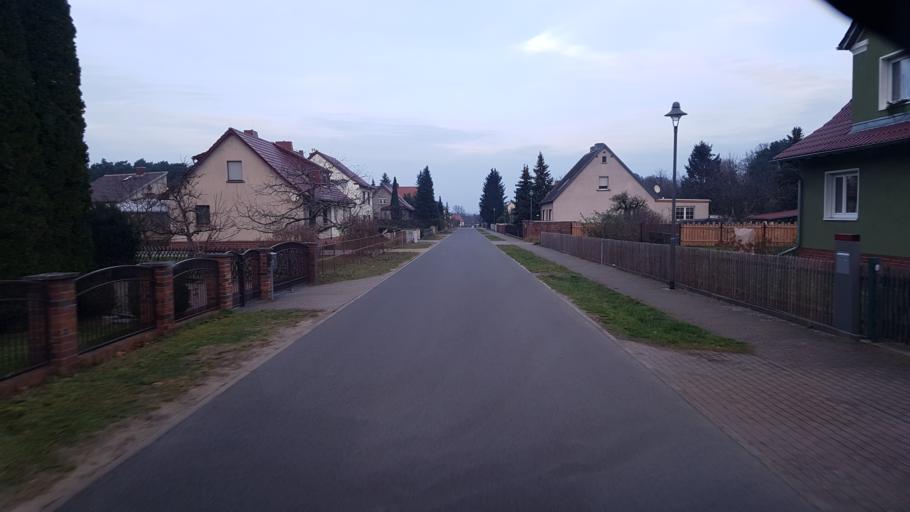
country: DE
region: Brandenburg
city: Ziltendorf
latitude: 52.2013
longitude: 14.6172
